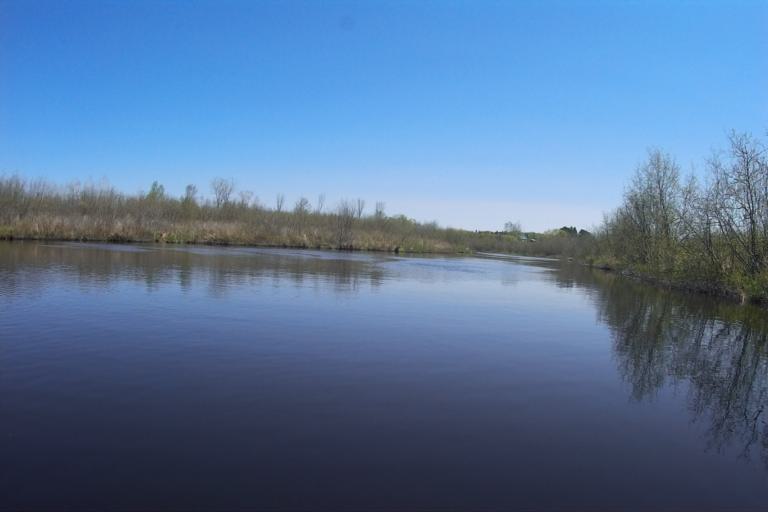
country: CA
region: Ontario
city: Powassan
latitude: 46.1584
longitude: -79.2528
